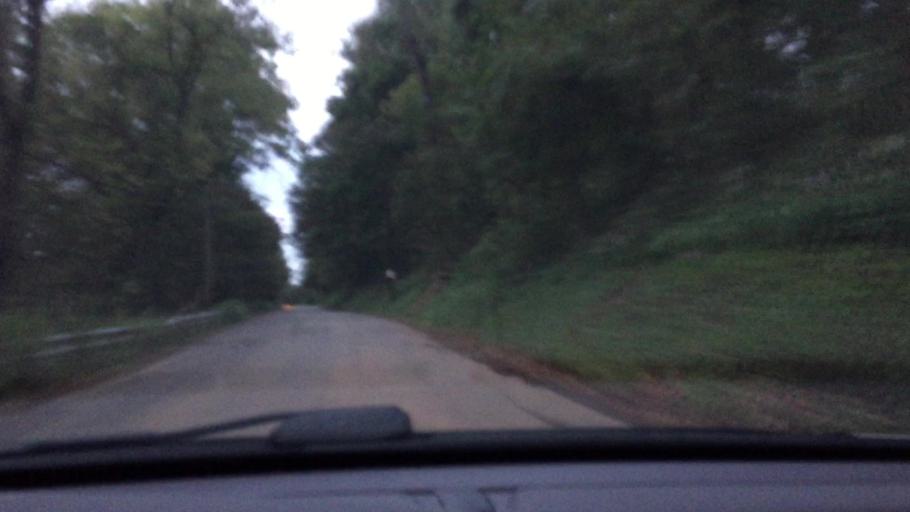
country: US
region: Pennsylvania
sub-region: Westmoreland County
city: West Newton
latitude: 40.2137
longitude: -79.7822
